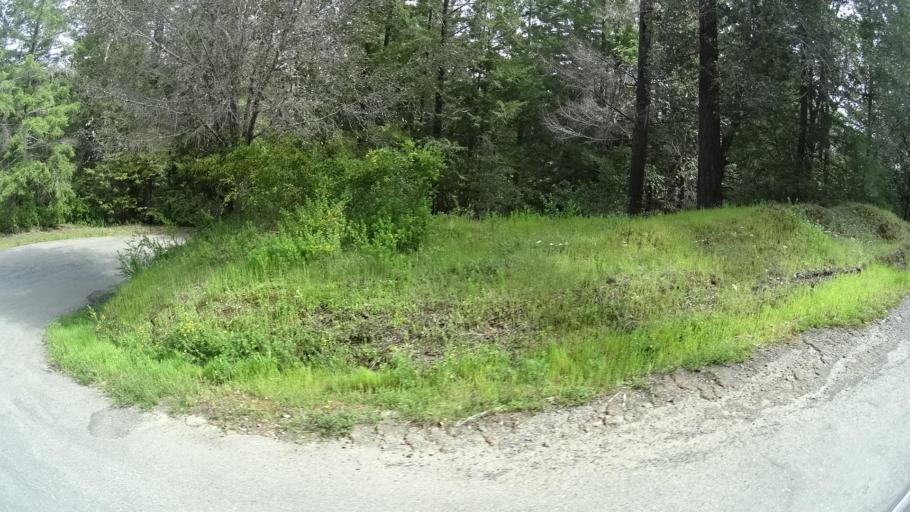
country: US
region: California
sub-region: Humboldt County
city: Redway
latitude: 40.0672
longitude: -123.8317
